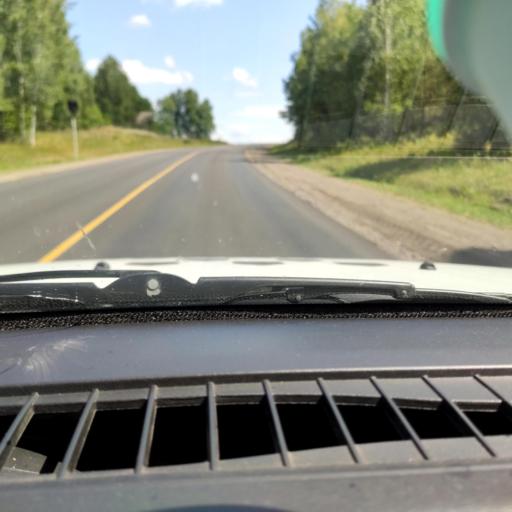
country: RU
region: Bashkortostan
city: Verkhniye Kigi
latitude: 55.3196
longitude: 58.7219
